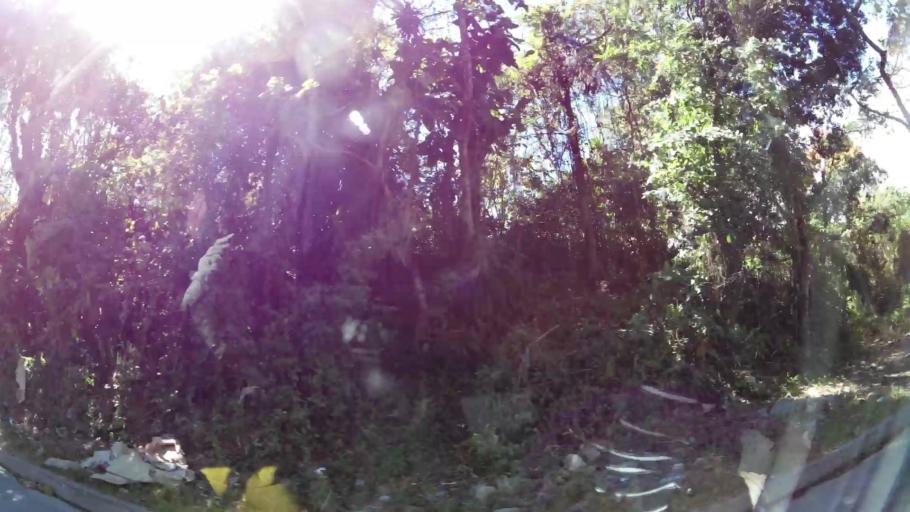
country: SV
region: San Salvador
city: Apopa
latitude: 13.8115
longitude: -89.1742
